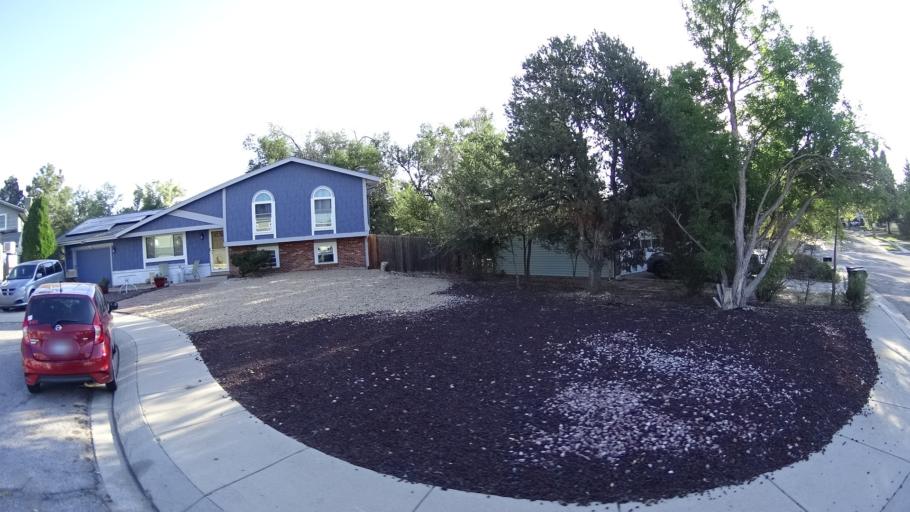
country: US
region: Colorado
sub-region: El Paso County
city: Cimarron Hills
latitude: 38.8854
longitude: -104.7502
